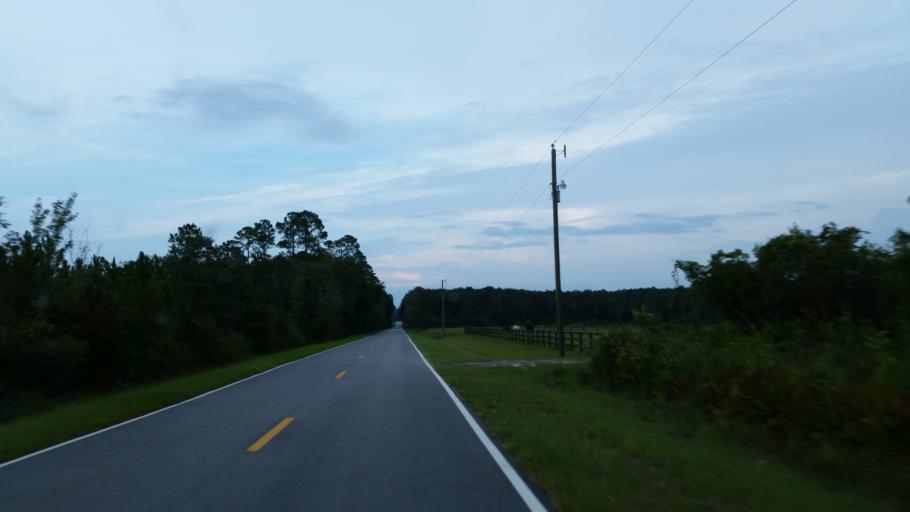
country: US
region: Georgia
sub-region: Lowndes County
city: Valdosta
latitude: 30.7458
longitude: -83.2428
